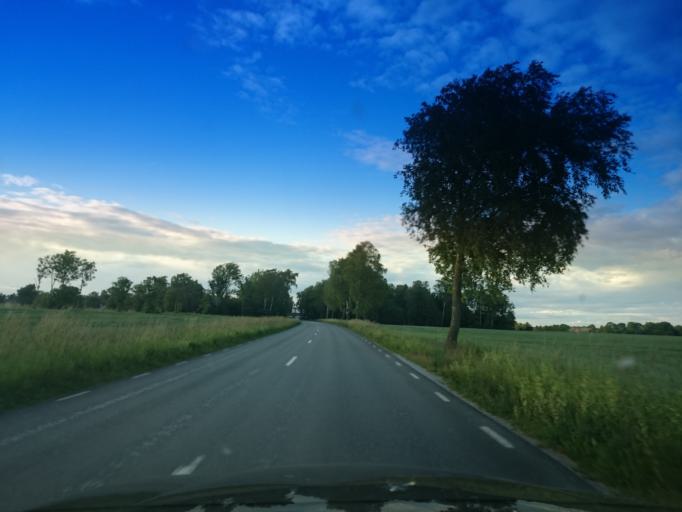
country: SE
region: Gotland
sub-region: Gotland
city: Hemse
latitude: 57.3149
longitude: 18.3840
